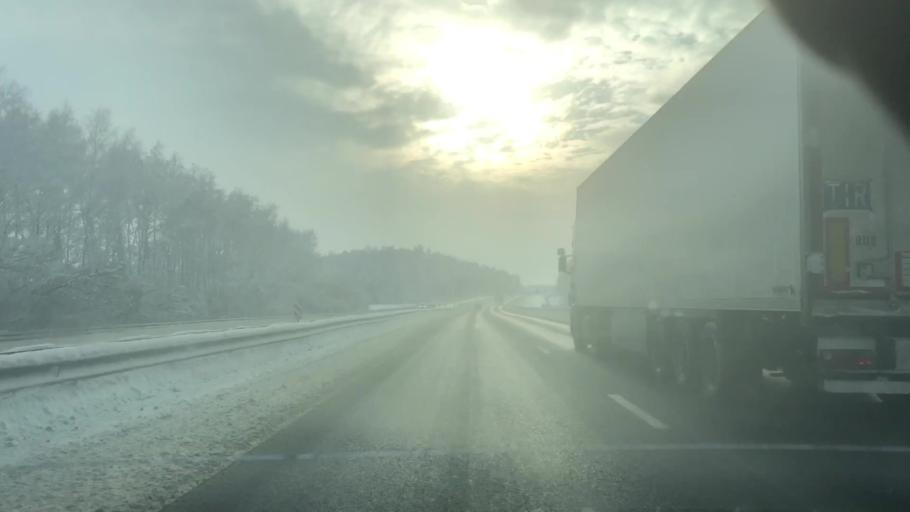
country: RU
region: Tula
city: Venev
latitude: 54.3864
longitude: 38.1539
